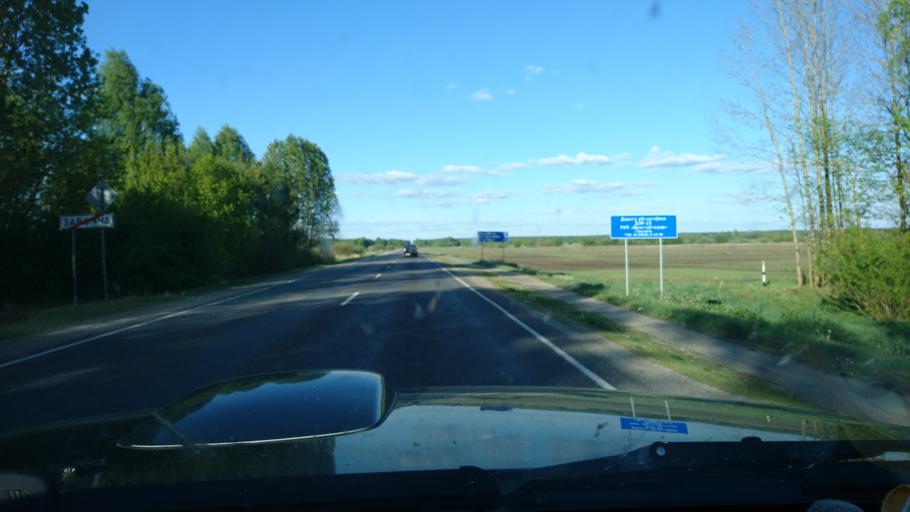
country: BY
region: Brest
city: Byaroza
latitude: 52.5492
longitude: 25.0145
